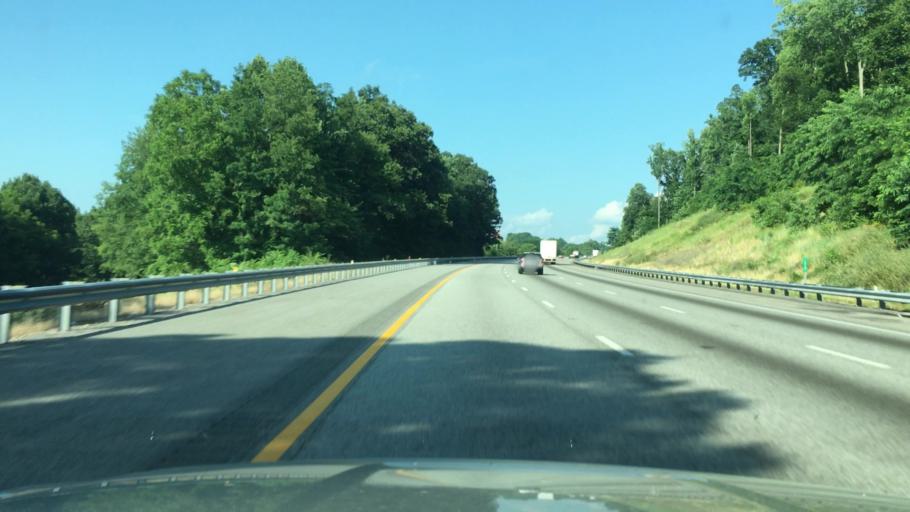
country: US
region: Virginia
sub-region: Rockbridge County
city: East Lexington
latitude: 37.8673
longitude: -79.3330
